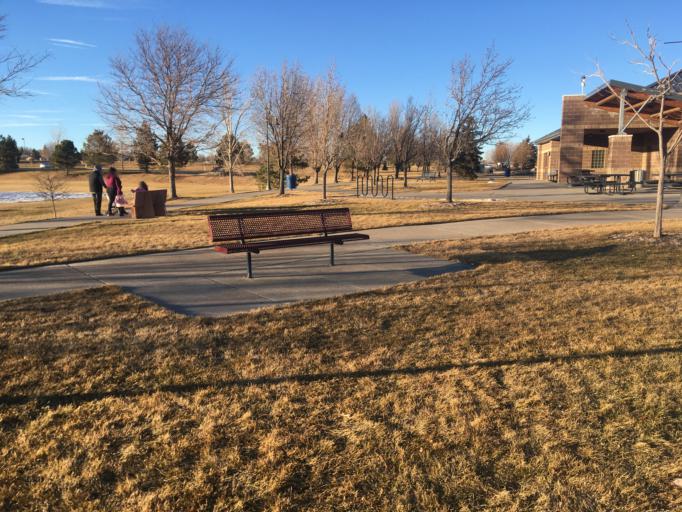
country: US
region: Colorado
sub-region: Broomfield County
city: Broomfield
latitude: 39.9348
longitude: -105.0492
